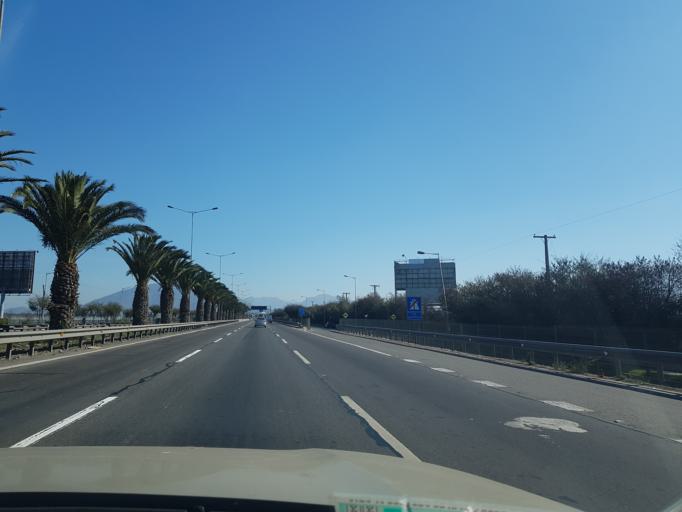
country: CL
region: Santiago Metropolitan
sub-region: Provincia de Santiago
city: Lo Prado
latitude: -33.4007
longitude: -70.7772
